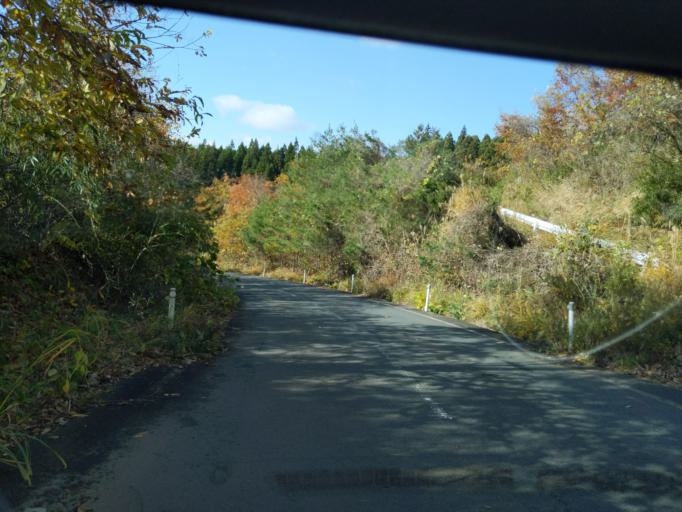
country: JP
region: Iwate
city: Mizusawa
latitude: 39.0356
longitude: 141.0796
